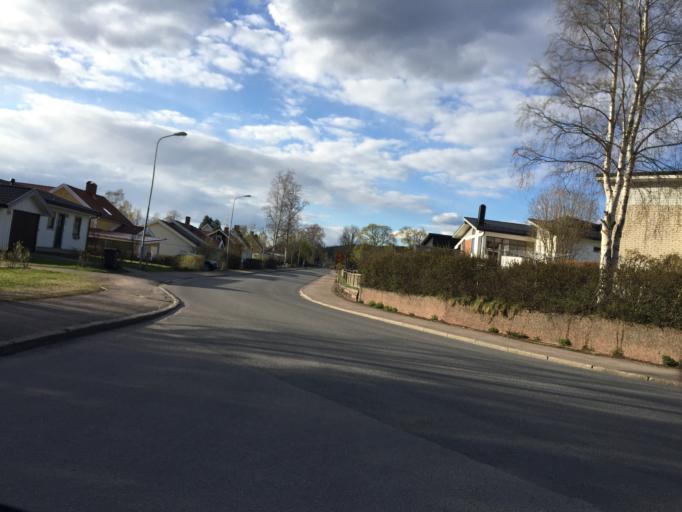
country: SE
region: Dalarna
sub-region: Ludvika Kommun
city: Ludvika
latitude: 60.1196
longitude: 15.1938
